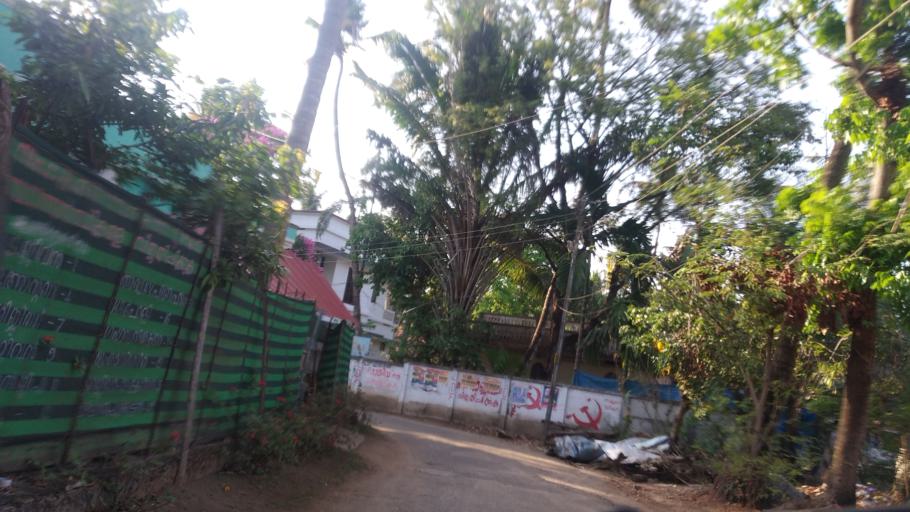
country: IN
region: Kerala
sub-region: Thrissur District
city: Kodungallur
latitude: 10.1387
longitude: 76.2018
